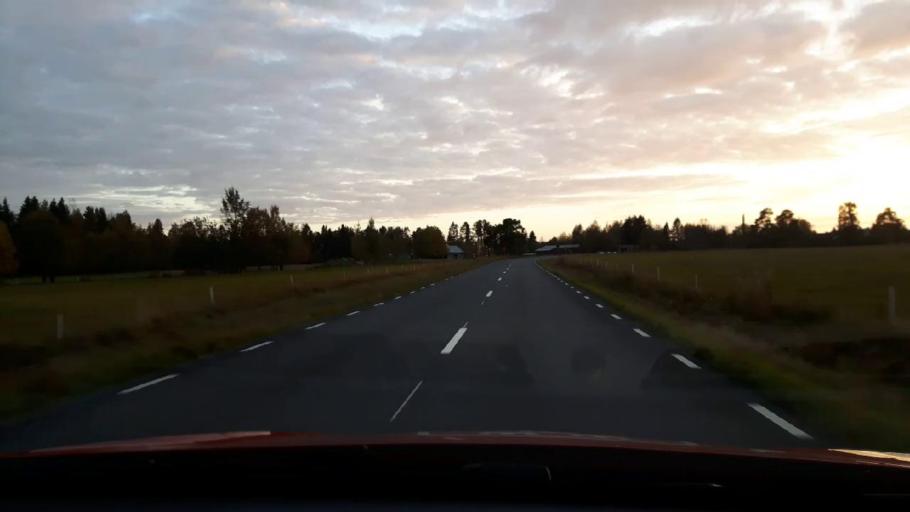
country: SE
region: Jaemtland
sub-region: OEstersunds Kommun
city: Ostersund
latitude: 63.2431
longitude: 14.5810
